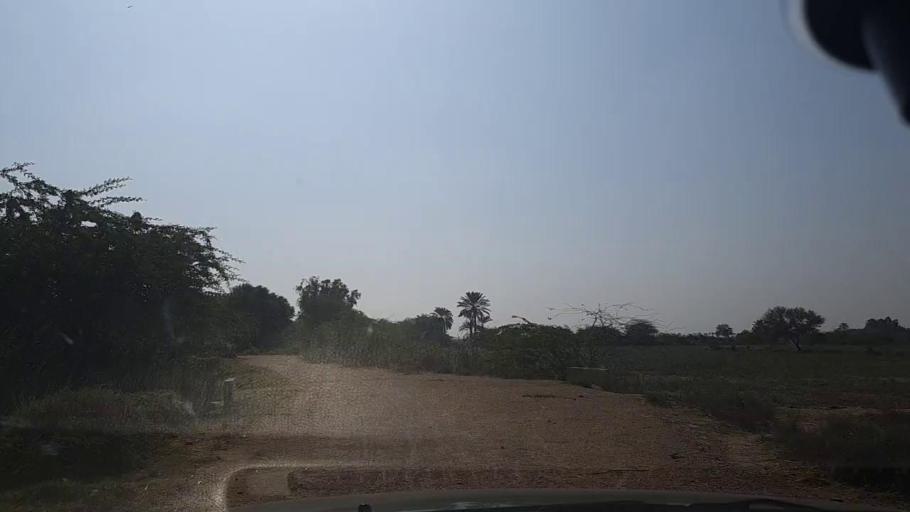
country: PK
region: Sindh
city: Chuhar Jamali
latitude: 24.5194
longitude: 67.8904
